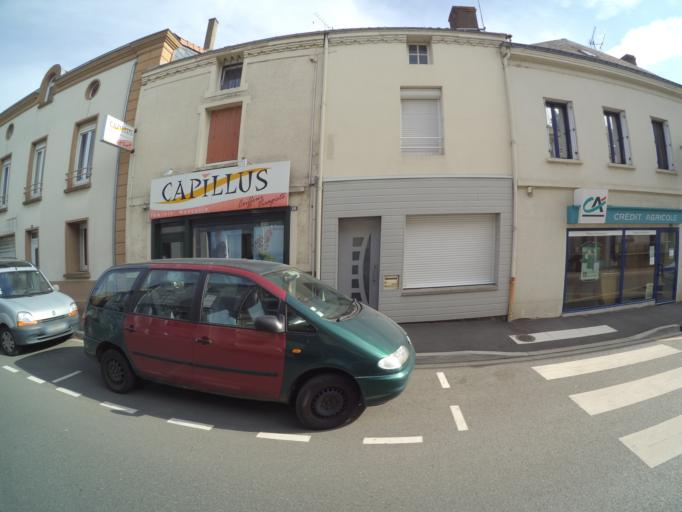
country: FR
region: Pays de la Loire
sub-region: Departement de Maine-et-Loire
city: Geste
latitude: 47.1808
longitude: -1.1113
